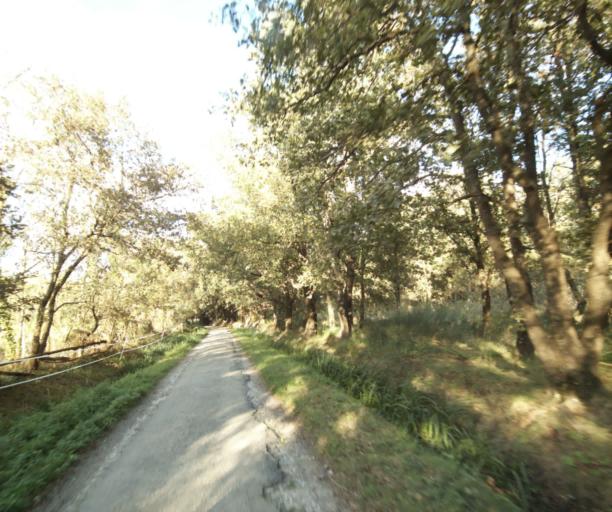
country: FR
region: Languedoc-Roussillon
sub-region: Departement des Pyrenees-Orientales
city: Argelers
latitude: 42.5637
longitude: 3.0199
